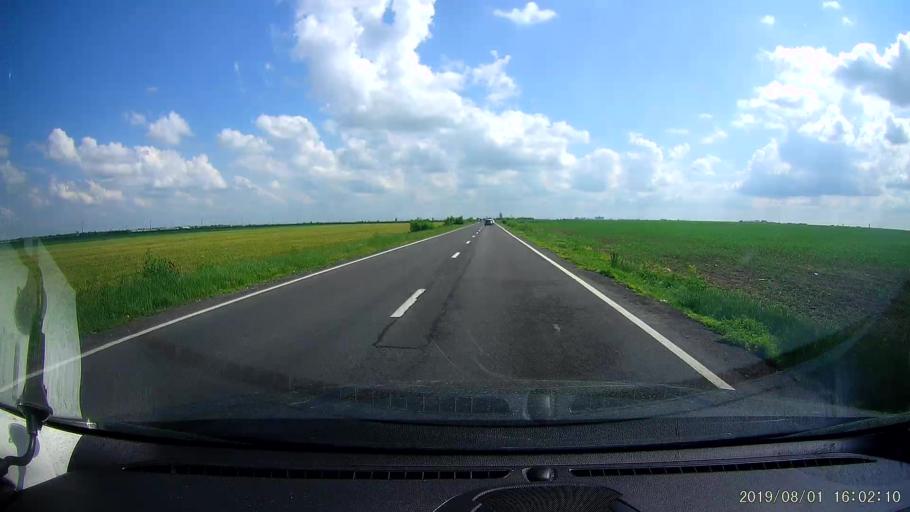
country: RO
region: Ialomita
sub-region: Comuna Ciulnita
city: Ciulnita
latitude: 44.4950
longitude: 27.3883
